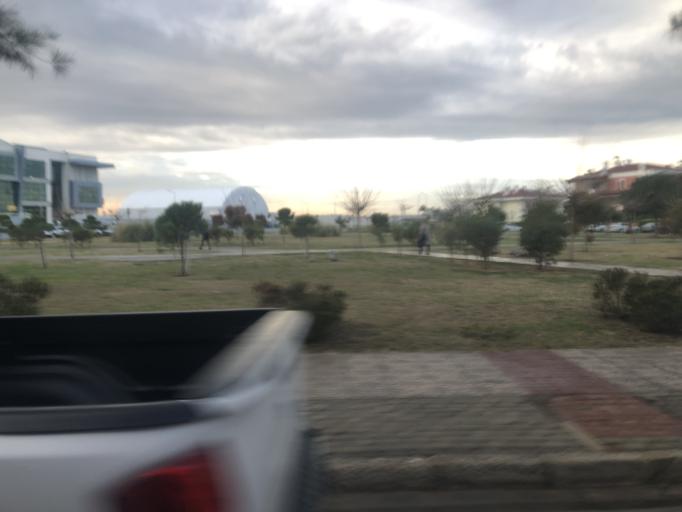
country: TR
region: Izmir
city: Karsiyaka
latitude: 38.4692
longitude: 27.0706
